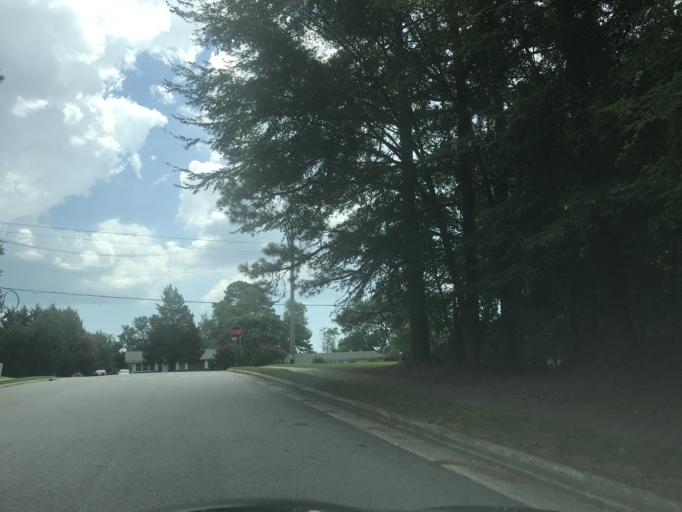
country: US
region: North Carolina
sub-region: Wake County
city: Wake Forest
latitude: 35.9571
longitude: -78.5248
